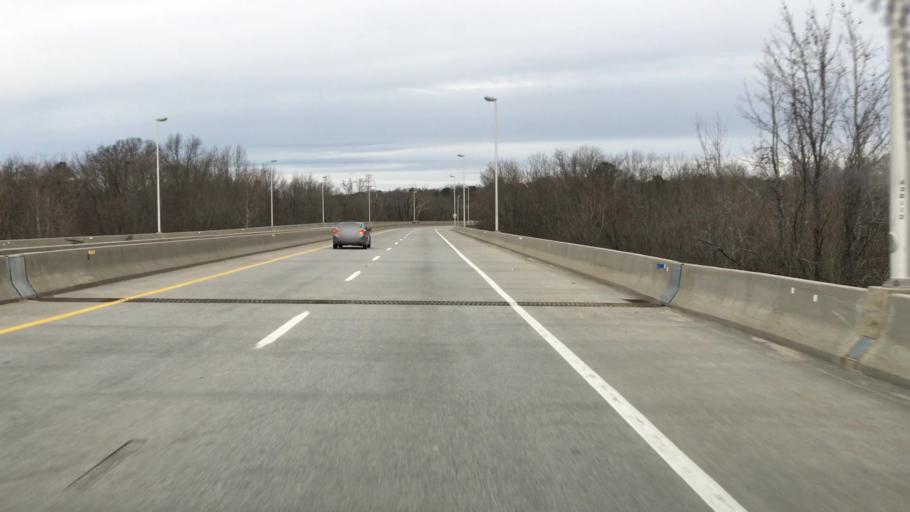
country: US
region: Virginia
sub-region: Henrico County
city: Tuckahoe
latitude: 37.5616
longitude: -77.5742
